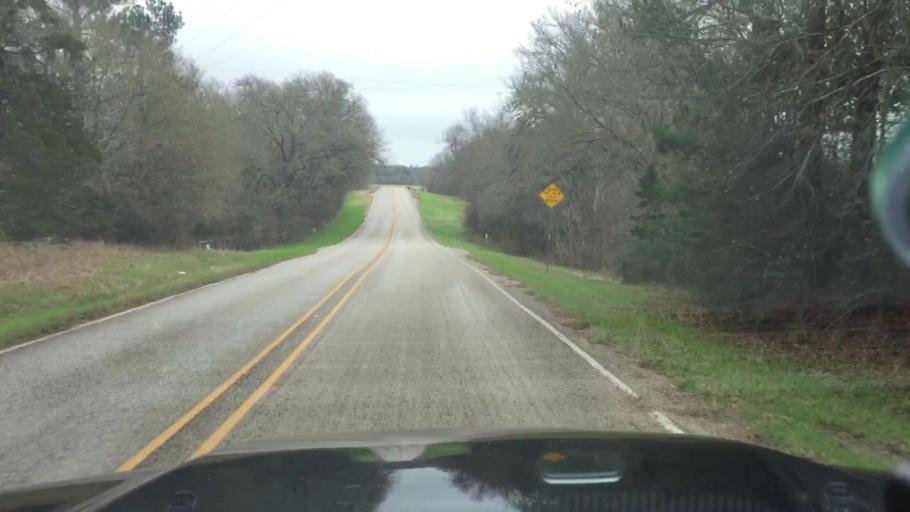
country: US
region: Texas
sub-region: Fayette County
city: La Grange
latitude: 30.0117
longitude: -96.9193
